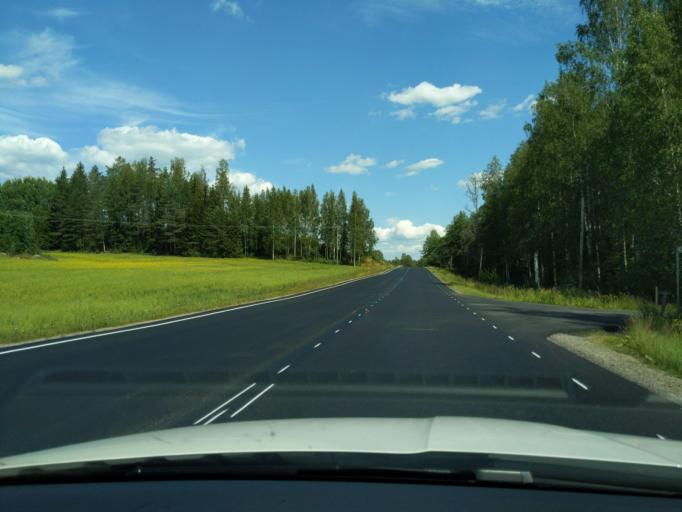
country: FI
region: Paijanne Tavastia
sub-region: Lahti
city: Nastola
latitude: 61.0961
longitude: 25.8977
